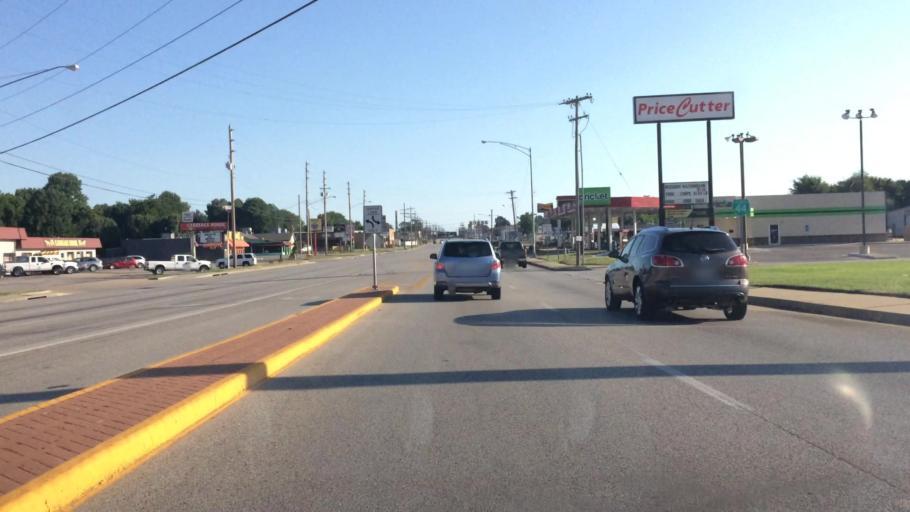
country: US
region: Missouri
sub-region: Greene County
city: Springfield
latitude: 37.2258
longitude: -93.2614
